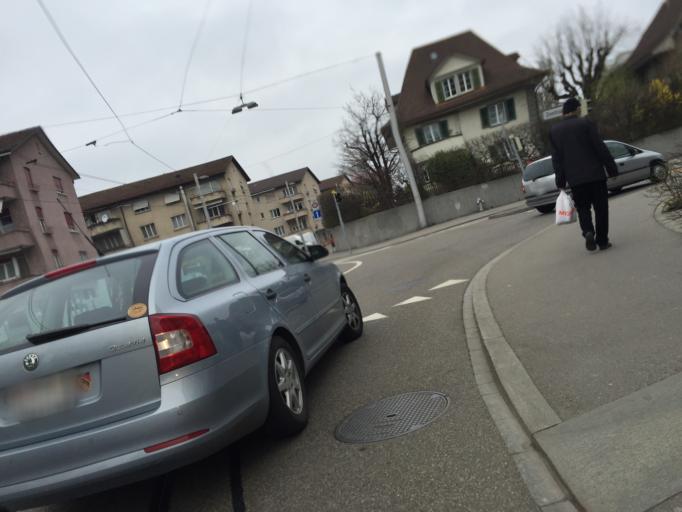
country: CH
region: Bern
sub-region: Bern-Mittelland District
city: Koniz
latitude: 46.9476
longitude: 7.3950
